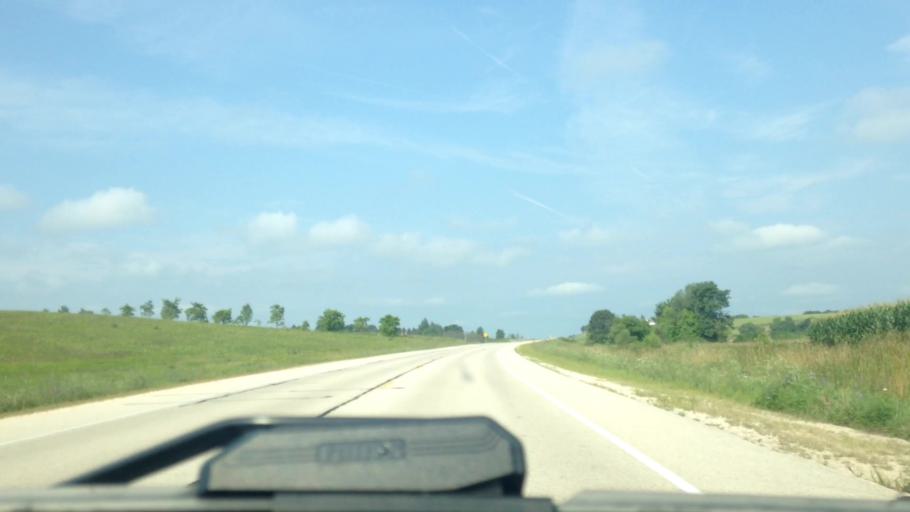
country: US
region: Wisconsin
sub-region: Dodge County
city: Theresa
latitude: 43.5366
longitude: -88.4254
